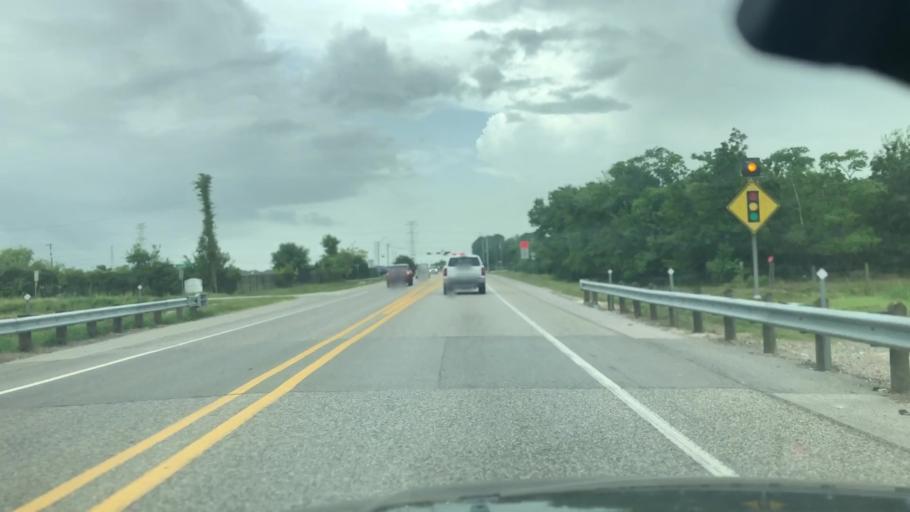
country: US
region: Texas
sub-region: Galveston County
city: Dickinson
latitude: 29.4867
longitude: -95.0611
